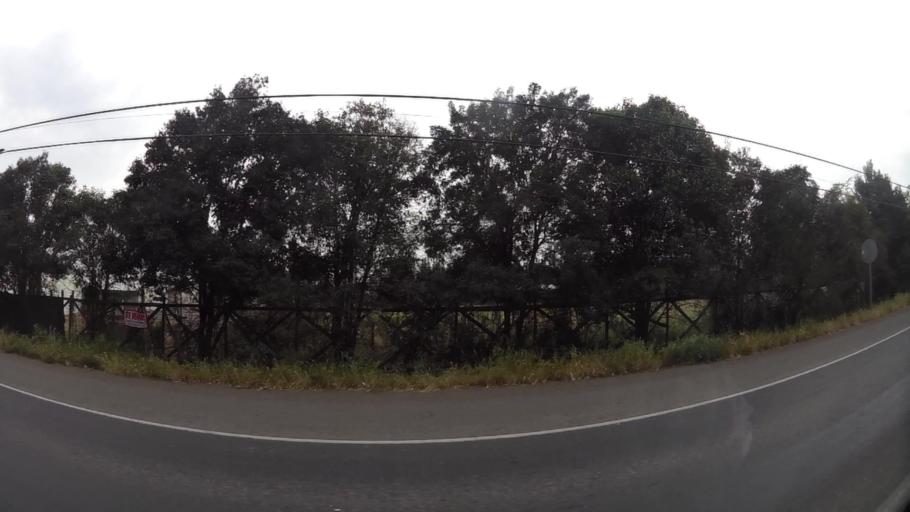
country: CL
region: Santiago Metropolitan
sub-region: Provincia de Chacabuco
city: Chicureo Abajo
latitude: -33.2491
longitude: -70.7140
